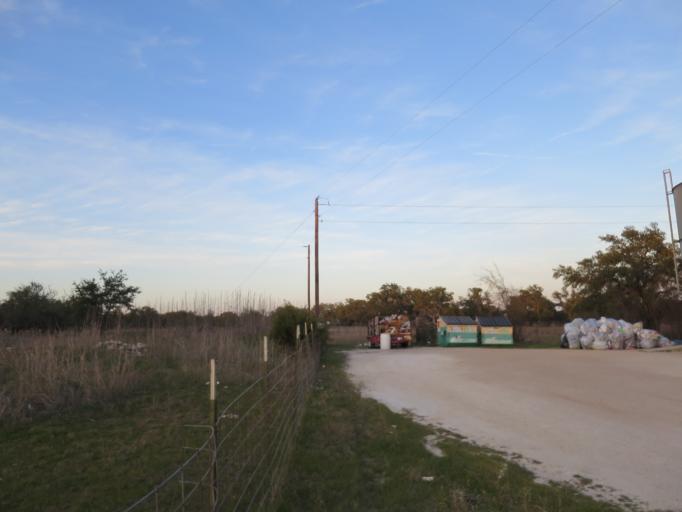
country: US
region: Texas
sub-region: Burnet County
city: Bertram
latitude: 30.7479
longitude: -98.0552
